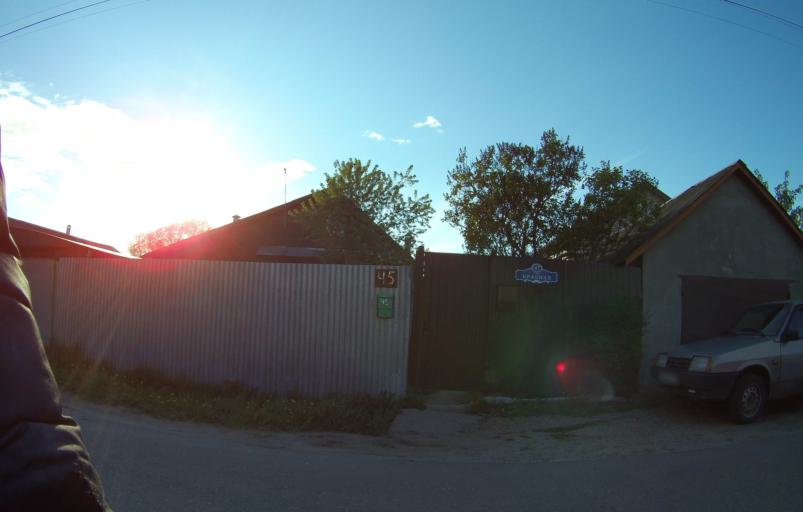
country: RU
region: Moskovskaya
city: Ramenskoye
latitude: 55.5868
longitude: 38.2635
